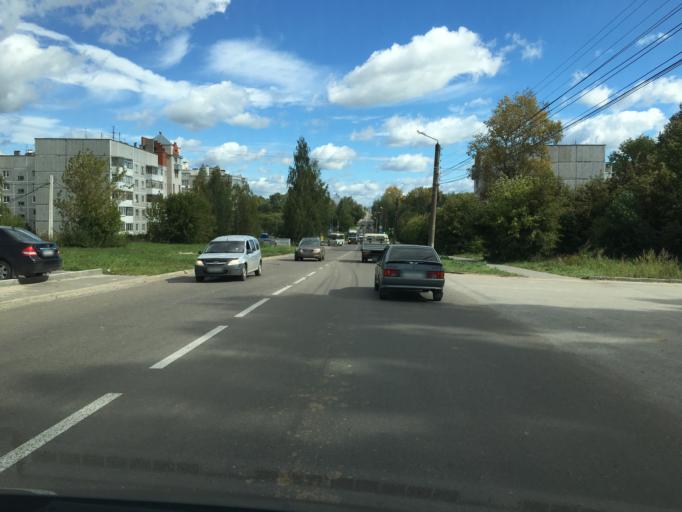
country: RU
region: Kaluga
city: Kaluga
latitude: 54.5431
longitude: 36.3226
